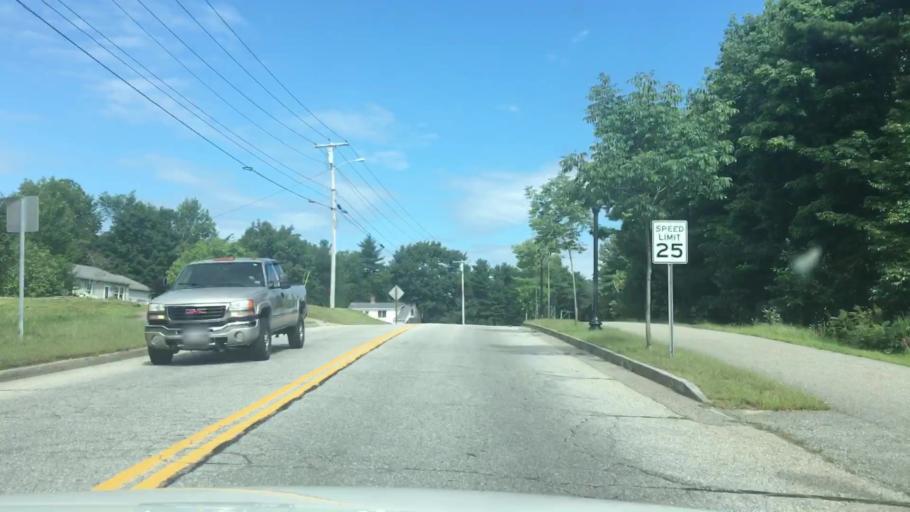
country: US
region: Maine
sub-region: Androscoggin County
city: Auburn
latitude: 44.0947
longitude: -70.2451
